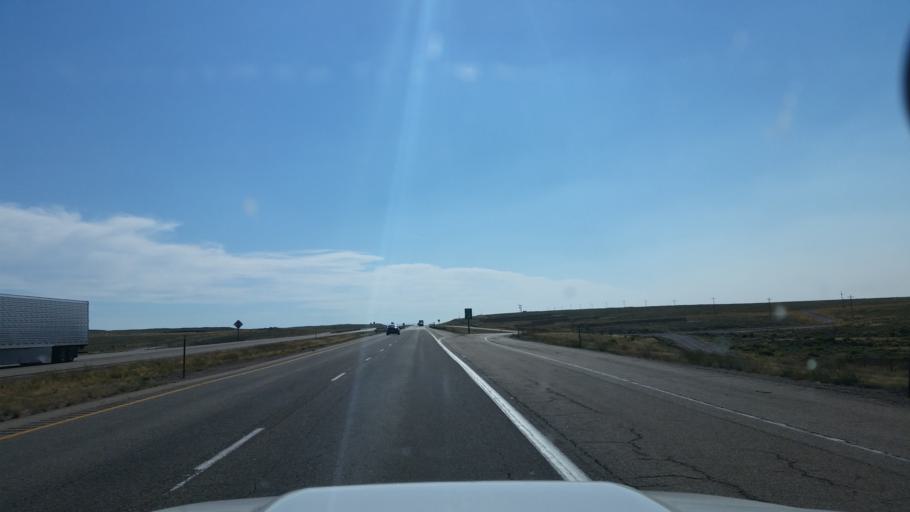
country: US
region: Wyoming
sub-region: Uinta County
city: Lyman
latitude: 41.4345
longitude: -110.1051
